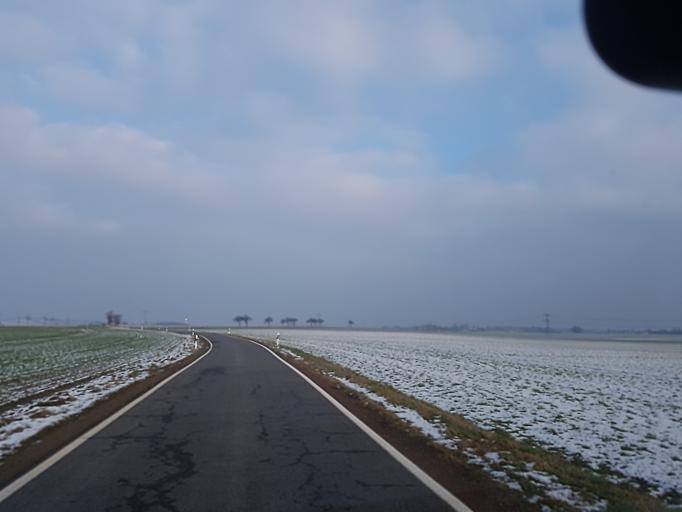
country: DE
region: Saxony
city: Oschatz
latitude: 51.3396
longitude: 13.1031
